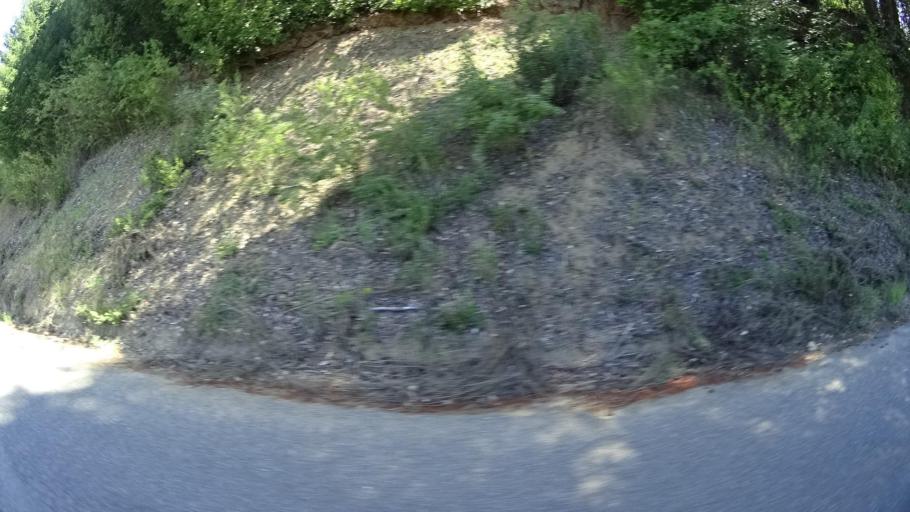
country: US
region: California
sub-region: Humboldt County
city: Redway
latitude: 40.1173
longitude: -123.9689
